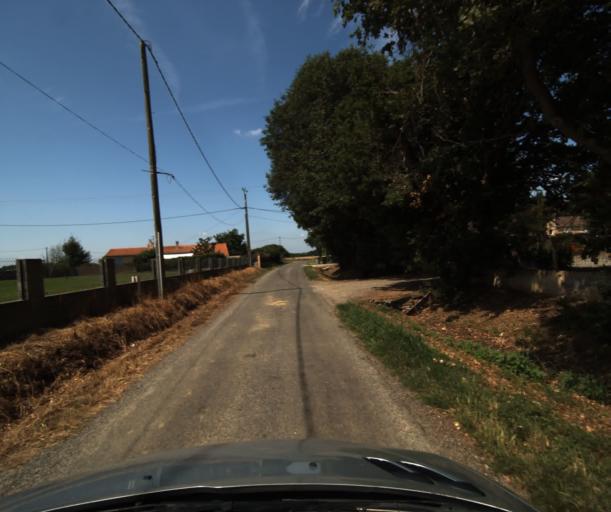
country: FR
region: Midi-Pyrenees
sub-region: Departement de la Haute-Garonne
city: Lherm
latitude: 43.4553
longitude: 1.1858
